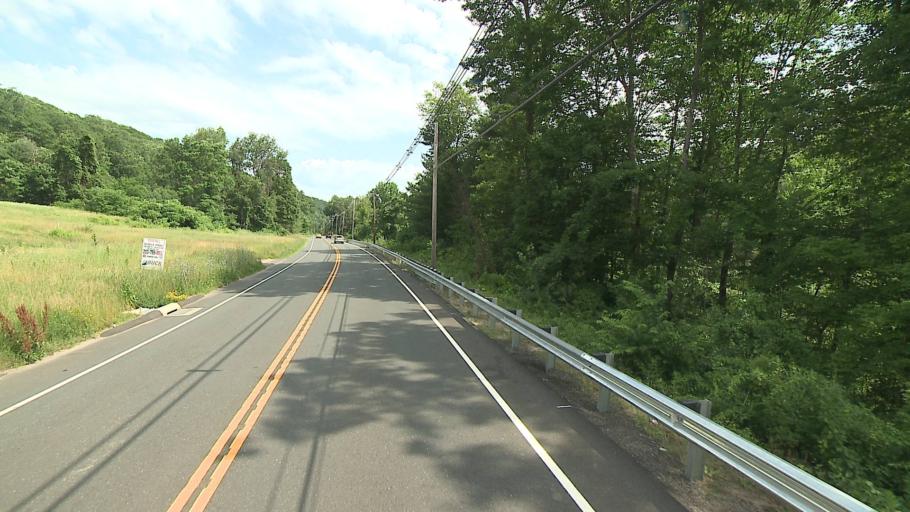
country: US
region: Connecticut
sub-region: Litchfield County
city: Winsted
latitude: 41.8861
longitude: -73.0745
